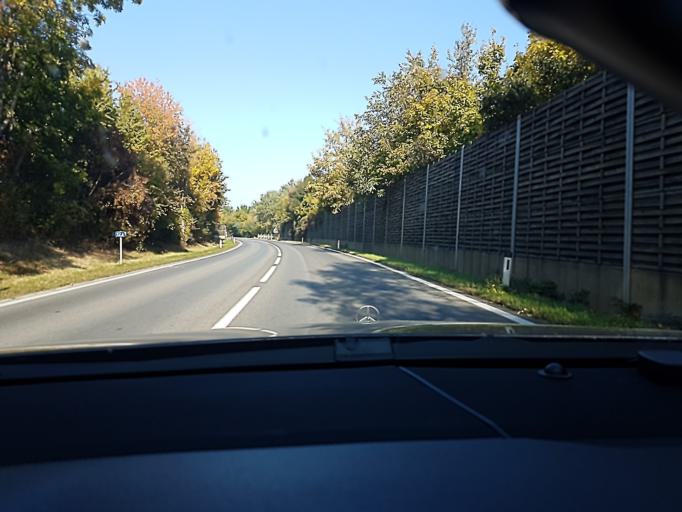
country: AT
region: Lower Austria
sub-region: Politischer Bezirk Modling
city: Laxenburg
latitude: 48.0784
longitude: 16.3570
